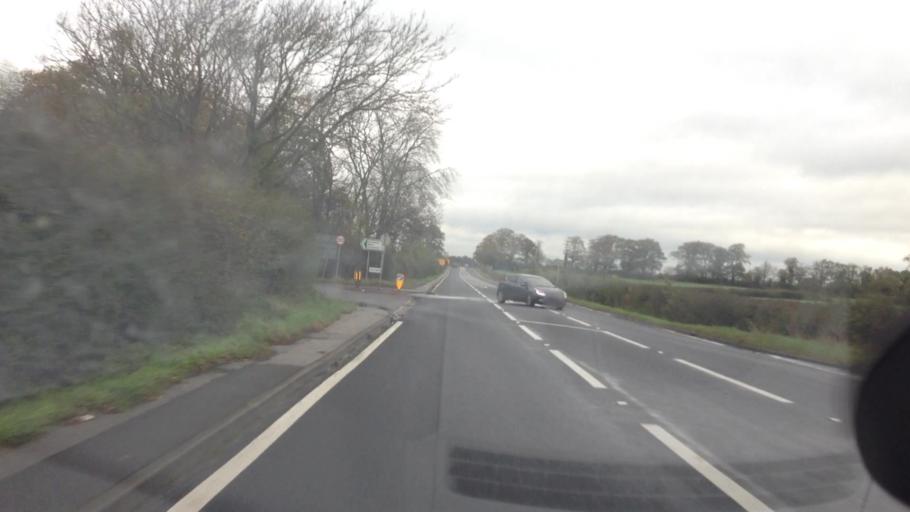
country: GB
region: England
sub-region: City and Borough of Leeds
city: Shadwell
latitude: 53.8495
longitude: -1.4646
